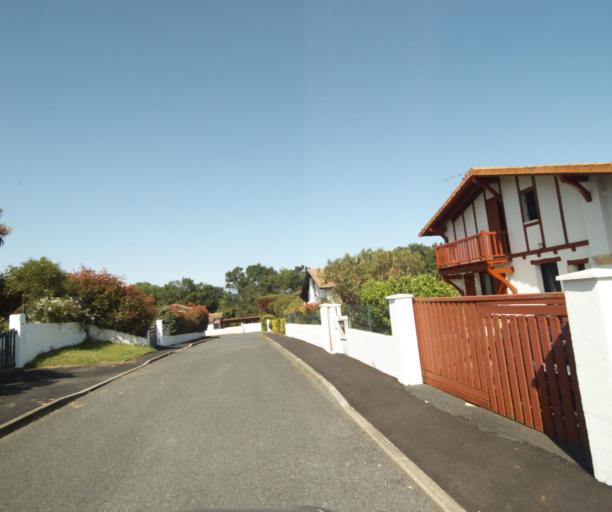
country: FR
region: Aquitaine
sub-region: Departement des Pyrenees-Atlantiques
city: Villefranque
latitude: 43.4581
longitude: -1.4523
